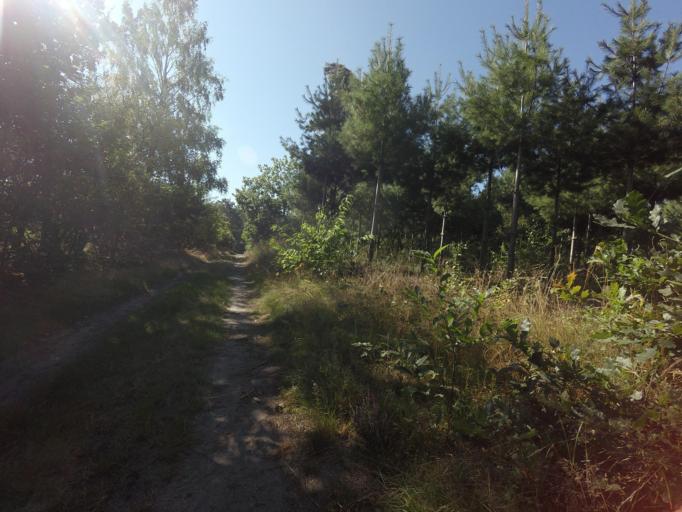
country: DE
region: Lower Saxony
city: Wielen
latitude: 52.5368
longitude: 6.7173
